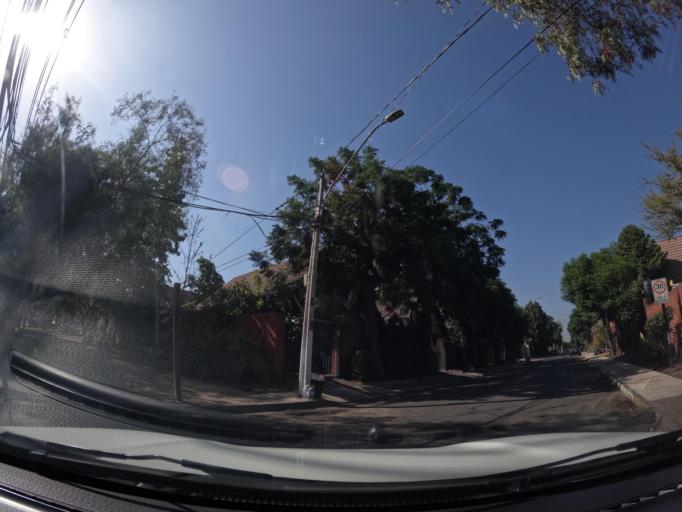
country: CL
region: Santiago Metropolitan
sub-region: Provincia de Santiago
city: Villa Presidente Frei, Nunoa, Santiago, Chile
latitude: -33.4796
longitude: -70.5566
